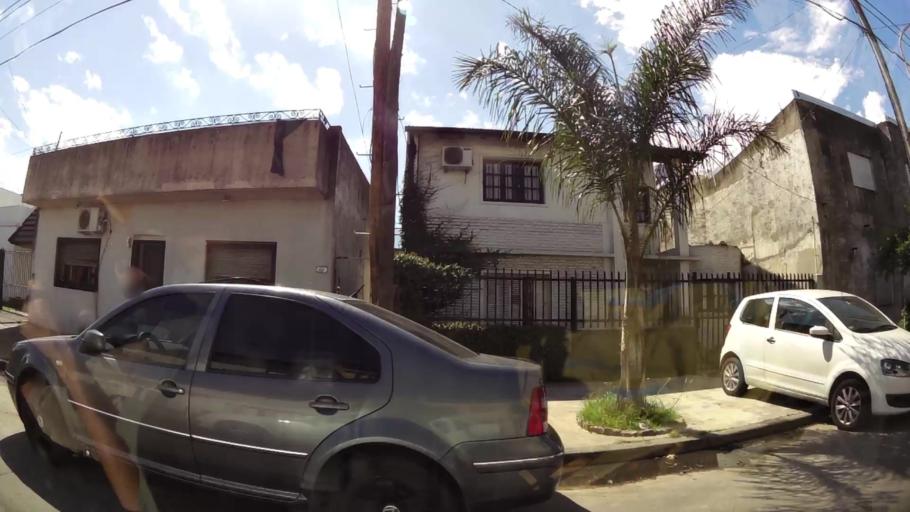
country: AR
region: Buenos Aires
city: San Justo
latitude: -34.6544
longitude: -58.5328
